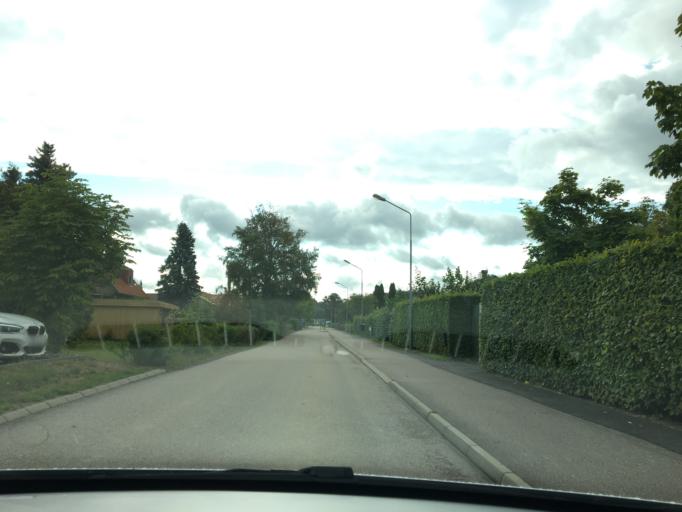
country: SE
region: Vaestra Goetaland
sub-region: Ale Kommun
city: Nodinge-Nol
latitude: 57.8902
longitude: 12.0465
